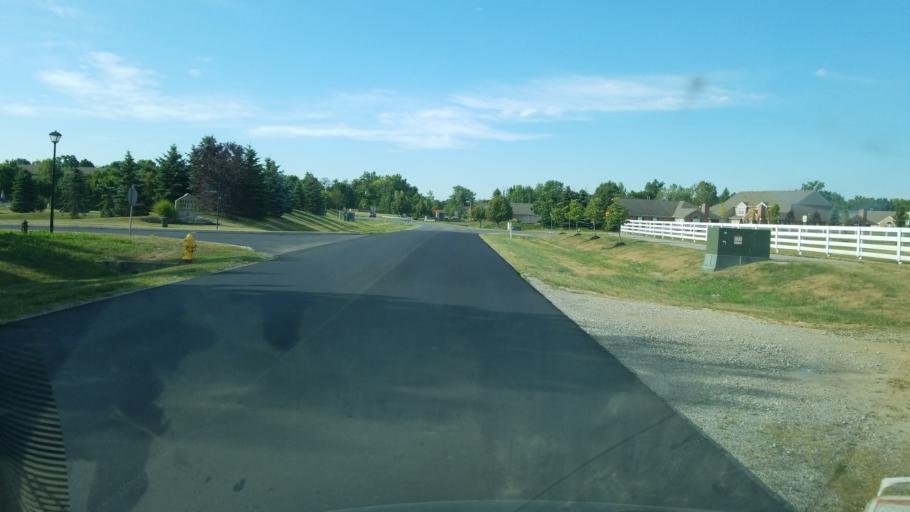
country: US
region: Ohio
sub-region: Delaware County
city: Lewis Center
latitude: 40.1731
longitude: -83.0142
